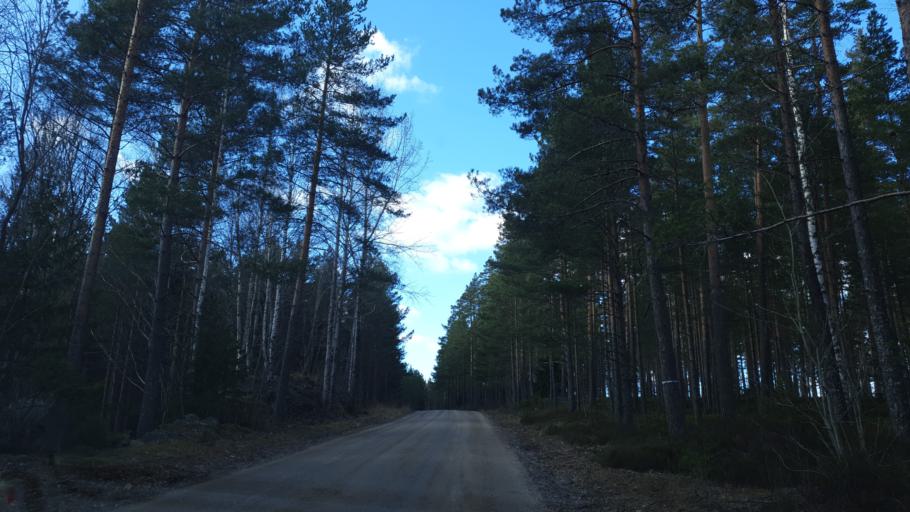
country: SE
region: OErebro
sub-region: Orebro Kommun
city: Garphyttan
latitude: 59.3536
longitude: 14.9838
